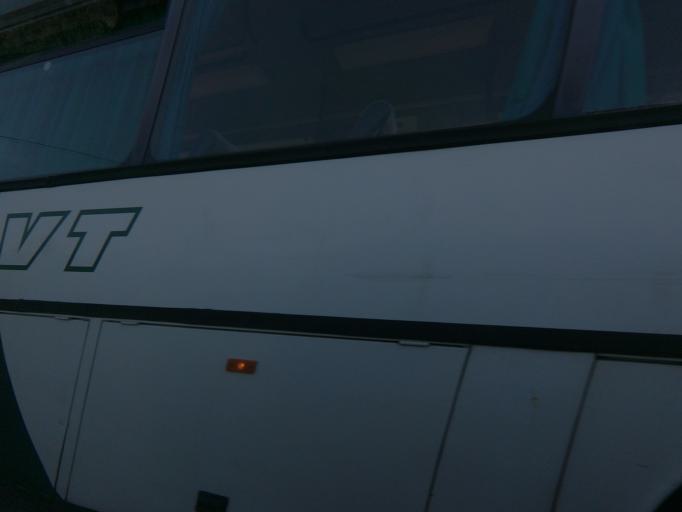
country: PT
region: Vila Real
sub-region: Sabrosa
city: Sabrosa
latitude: 41.2500
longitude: -7.4661
